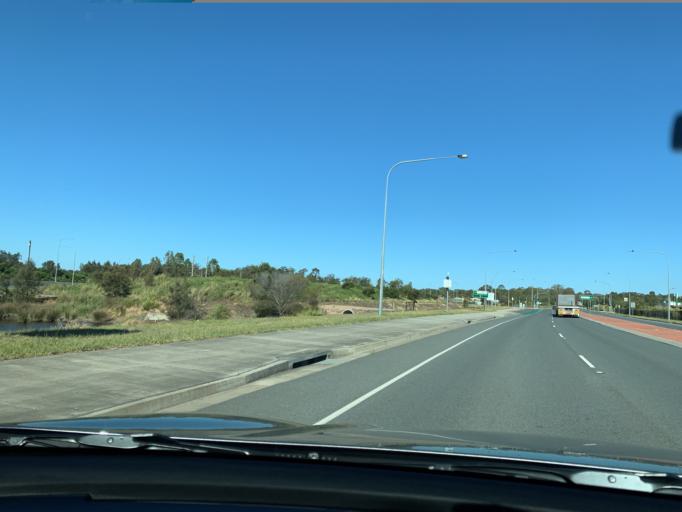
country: AU
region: Queensland
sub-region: Brisbane
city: Wynnum
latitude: -27.4249
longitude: 153.1504
